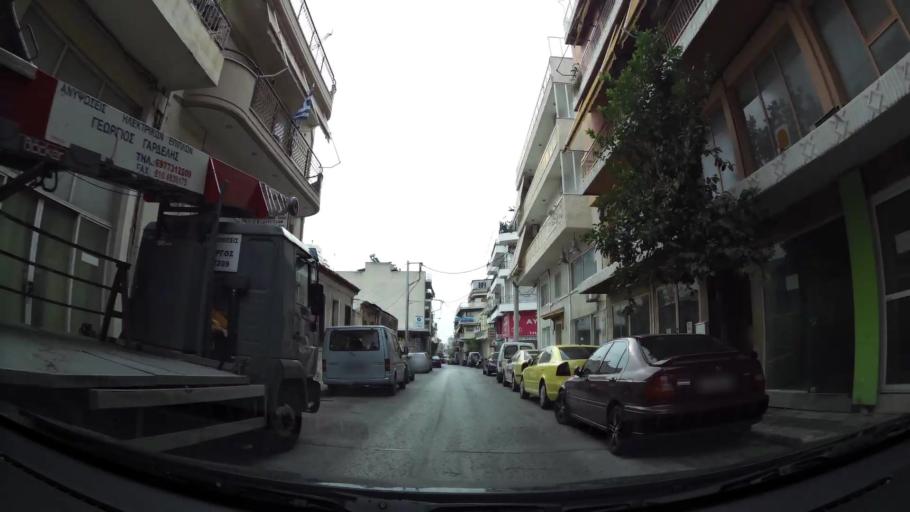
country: GR
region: Attica
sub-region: Nomos Piraios
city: Nikaia
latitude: 37.9597
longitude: 23.6499
